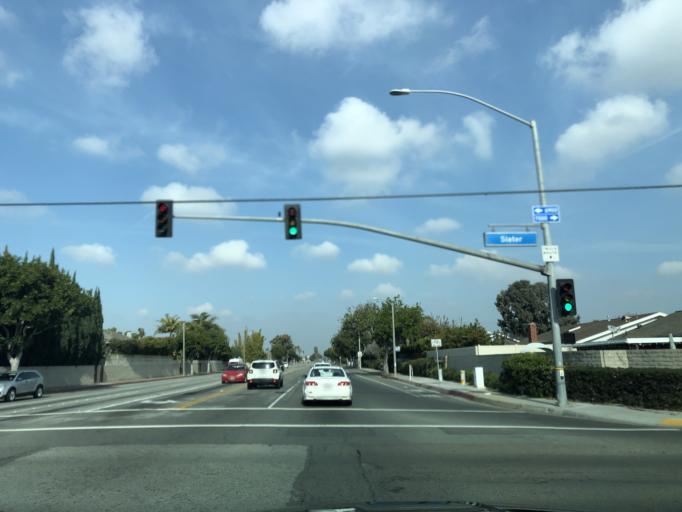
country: US
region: California
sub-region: Orange County
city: Midway City
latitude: 33.7082
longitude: -118.0063
